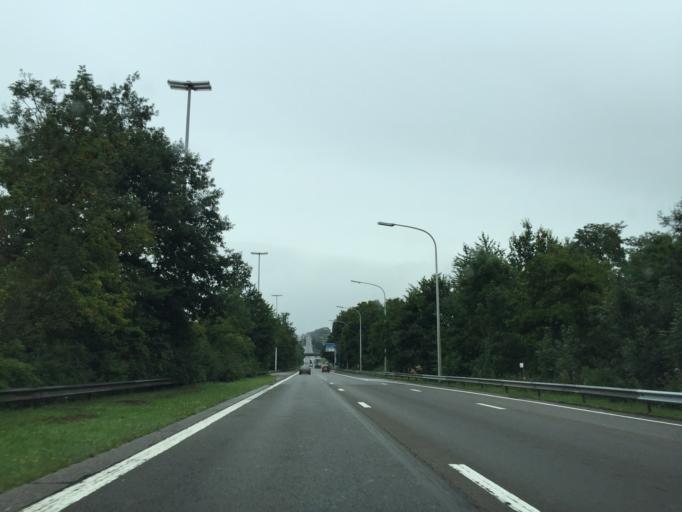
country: BE
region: Wallonia
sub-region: Province de Liege
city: Bassenge
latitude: 50.7454
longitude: 5.5750
